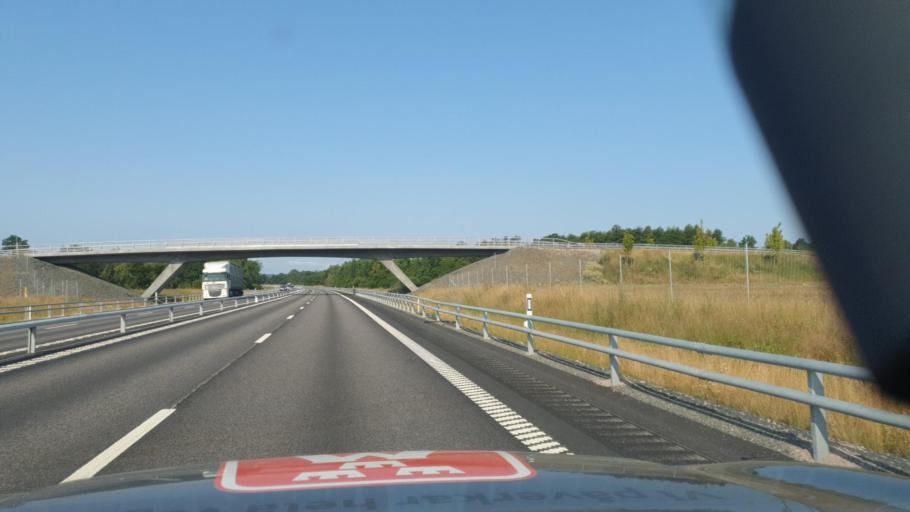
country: SE
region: Skane
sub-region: Kristianstads Kommun
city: Onnestad
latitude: 55.9610
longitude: 13.9561
